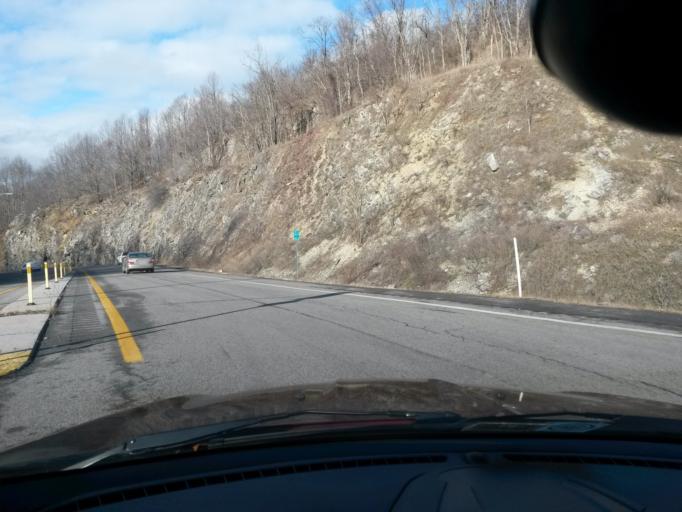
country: US
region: West Virginia
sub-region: Mercer County
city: Princeton
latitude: 37.2853
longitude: -81.1236
